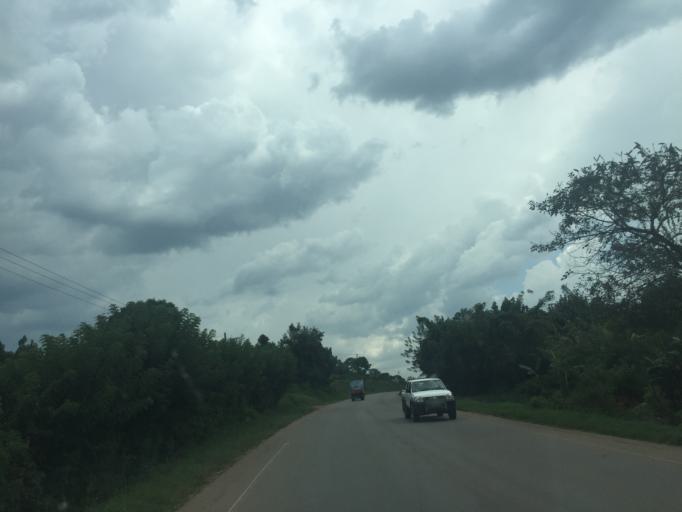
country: UG
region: Central Region
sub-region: Luwero District
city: Wobulenzi
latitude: 0.6740
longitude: 32.5280
